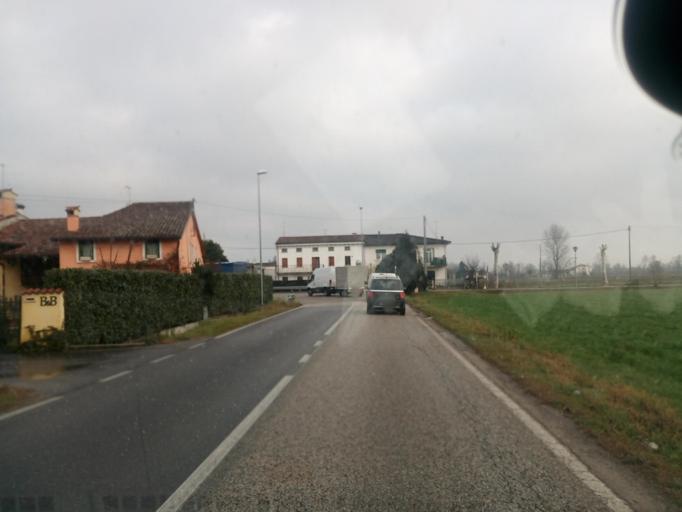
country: IT
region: Veneto
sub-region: Provincia di Vicenza
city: Bressanvido
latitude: 45.6627
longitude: 11.6425
